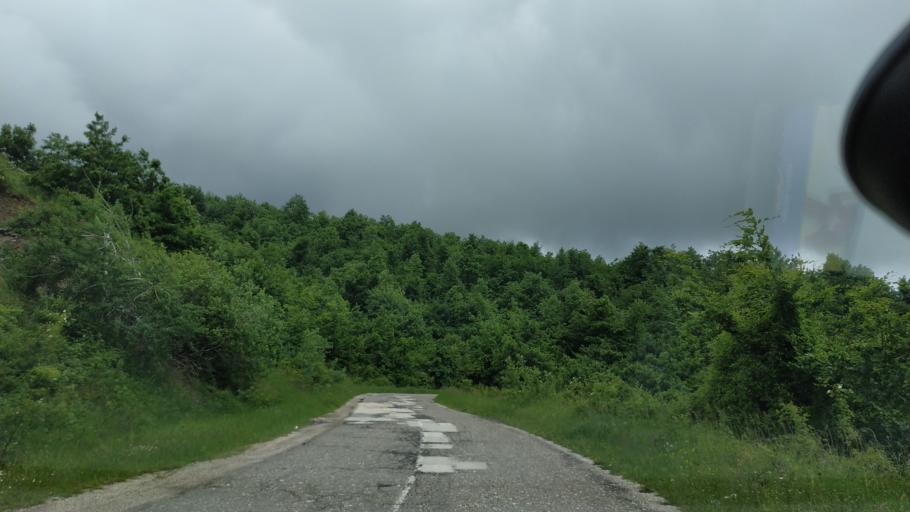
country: RS
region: Central Serbia
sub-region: Zajecarski Okrug
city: Soko Banja
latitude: 43.7180
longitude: 21.9447
